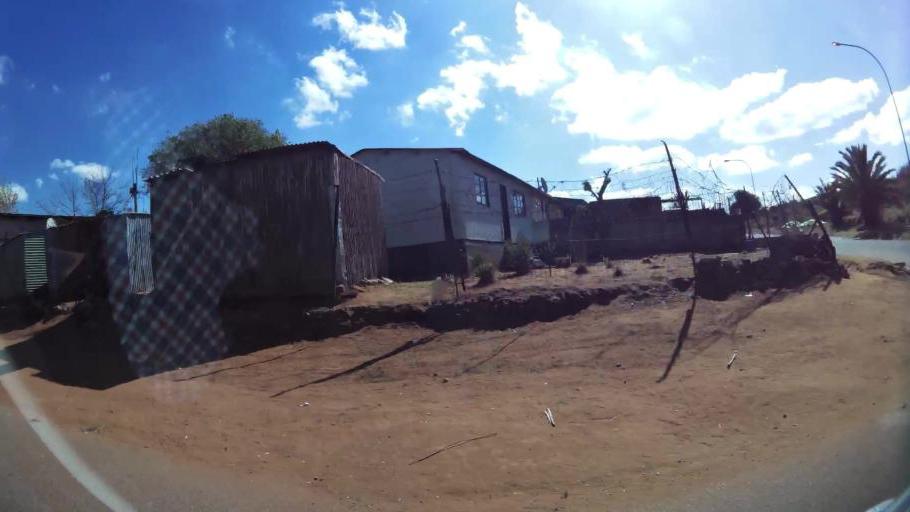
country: ZA
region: Gauteng
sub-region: City of Johannesburg Metropolitan Municipality
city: Soweto
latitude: -26.2231
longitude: 27.9119
